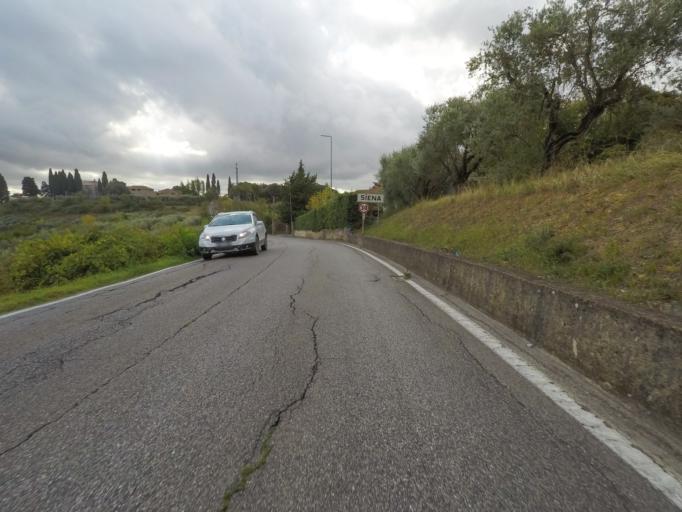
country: IT
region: Tuscany
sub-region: Provincia di Siena
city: Belverde
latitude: 43.3454
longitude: 11.3135
